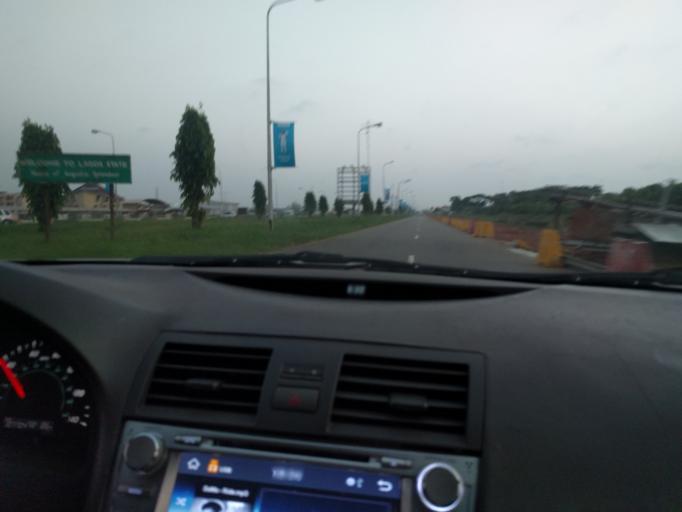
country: NG
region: Lagos
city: Oshodi
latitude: 6.5737
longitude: 3.3210
